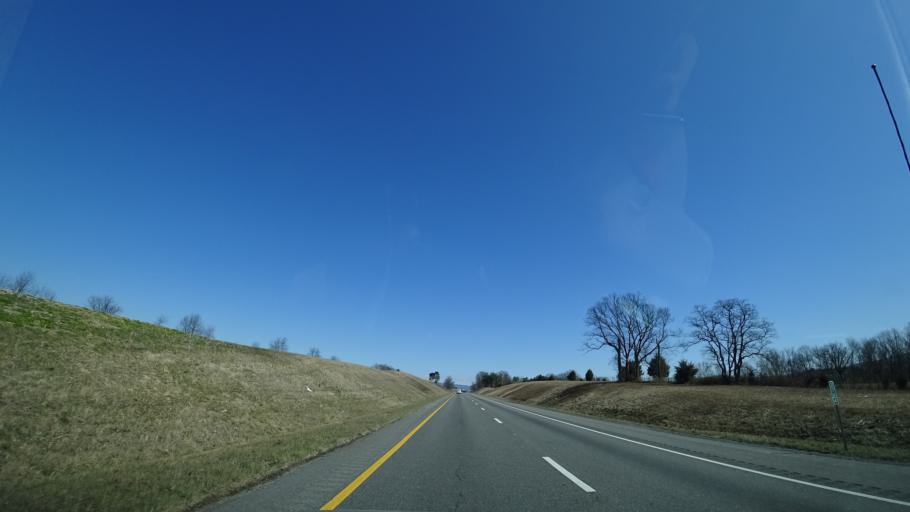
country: US
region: Virginia
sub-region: Shenandoah County
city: Edinburg
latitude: 38.7966
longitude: -78.6063
